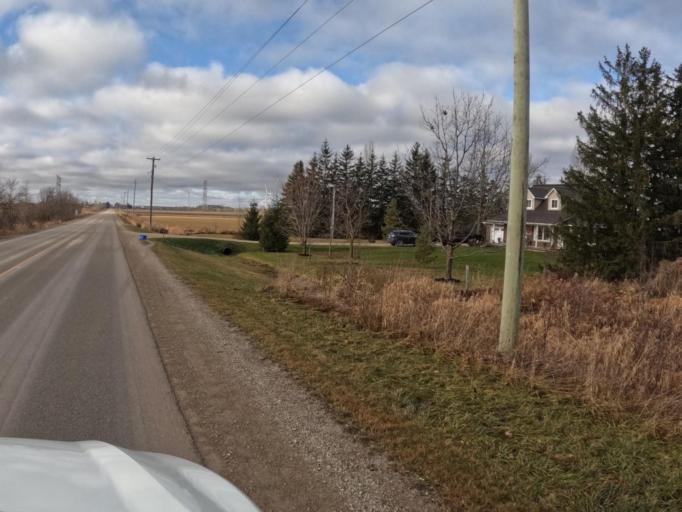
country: CA
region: Ontario
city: Shelburne
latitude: 43.8953
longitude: -80.3336
